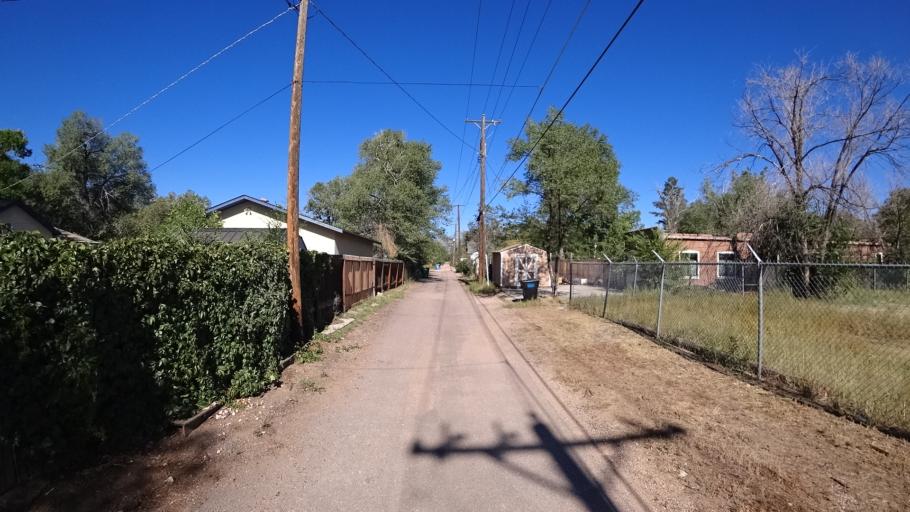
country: US
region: Colorado
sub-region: El Paso County
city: Colorado Springs
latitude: 38.8439
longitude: -104.8602
